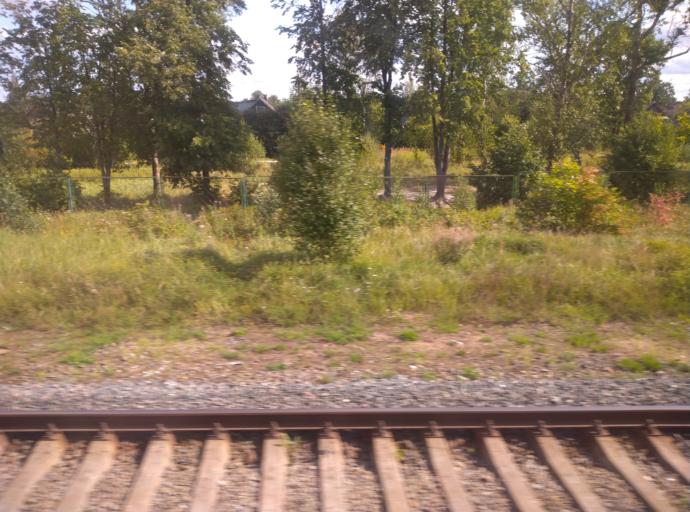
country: RU
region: Leningrad
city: Ul'yanovka
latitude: 59.6283
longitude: 30.7666
